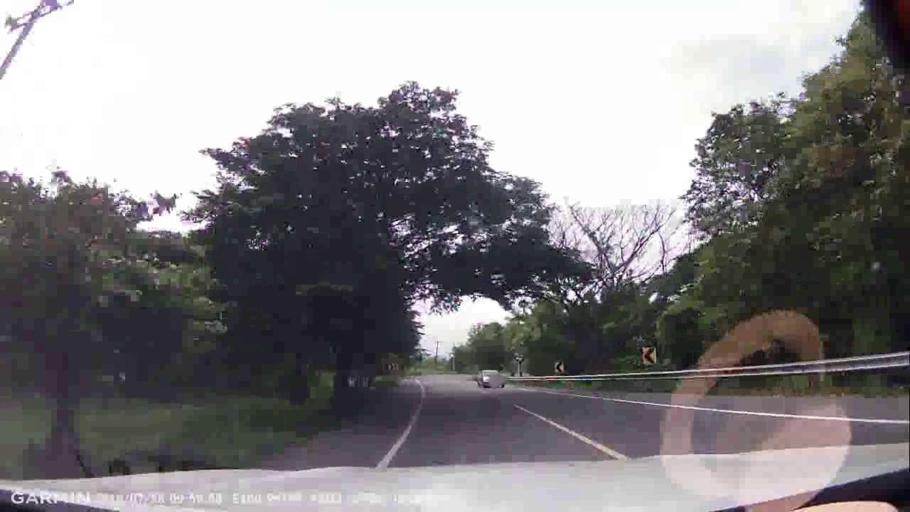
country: TH
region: Chon Buri
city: Si Racha
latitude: 13.2275
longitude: 100.9982
